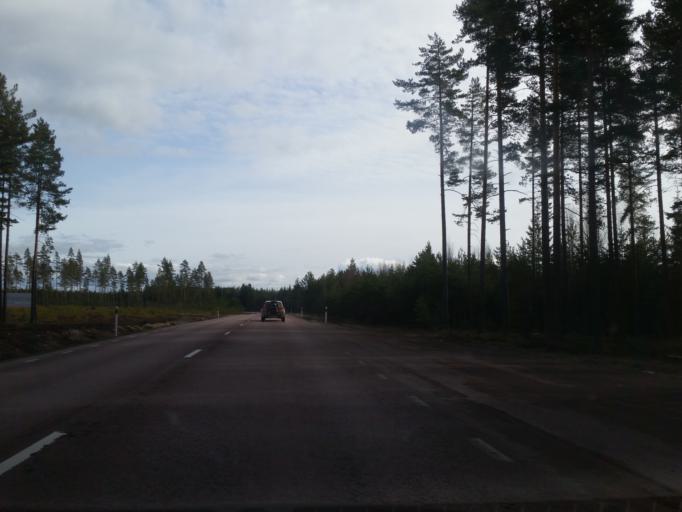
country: SE
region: Dalarna
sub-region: Leksand Municipality
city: Siljansnas
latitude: 60.9426
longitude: 14.7469
